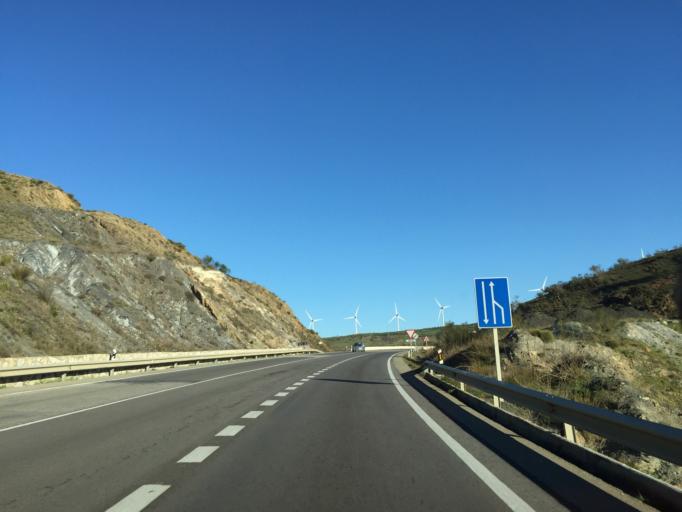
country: ES
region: Andalusia
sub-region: Provincia de Malaga
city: Carratraca
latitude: 36.8505
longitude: -4.8260
